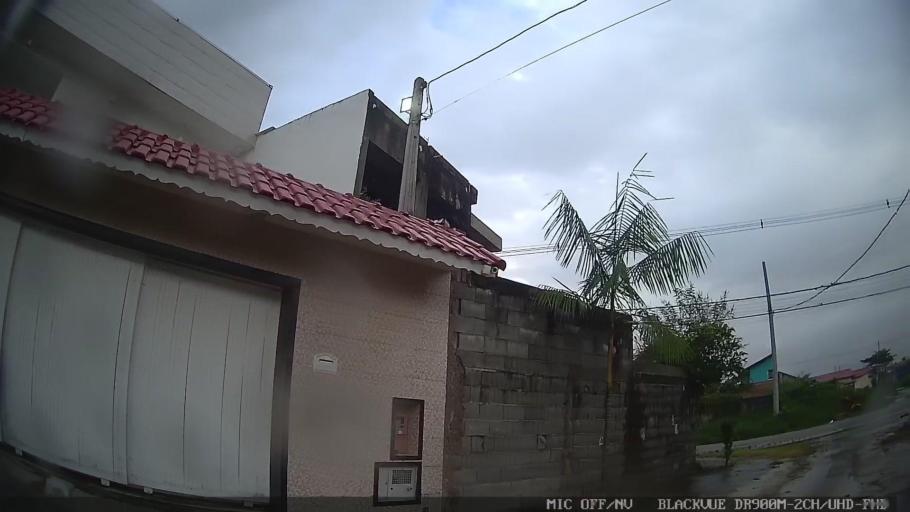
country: BR
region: Sao Paulo
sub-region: Itanhaem
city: Itanhaem
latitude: -24.1657
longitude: -46.7713
